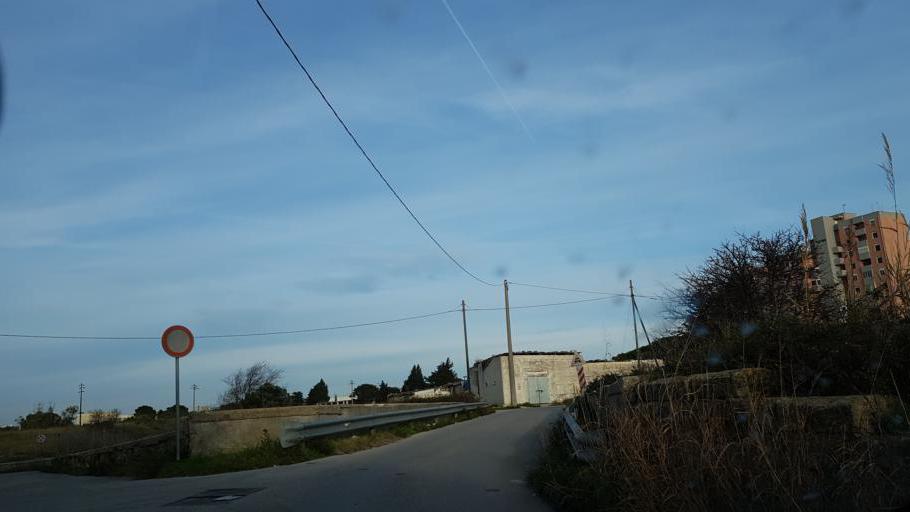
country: IT
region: Apulia
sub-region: Provincia di Brindisi
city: Brindisi
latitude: 40.6323
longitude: 17.9500
